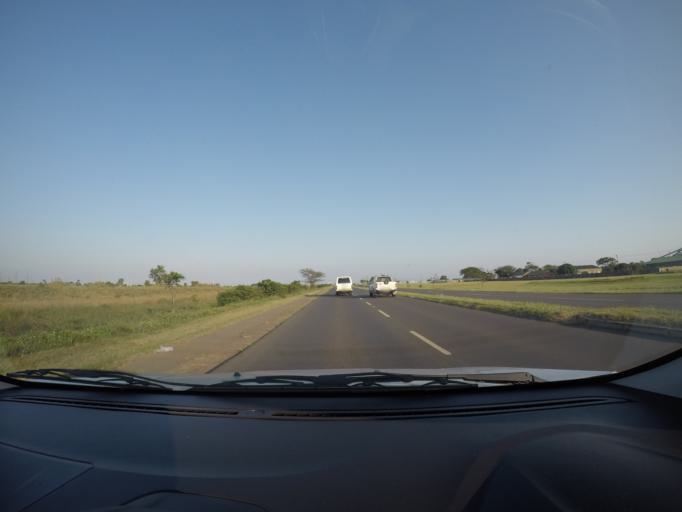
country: ZA
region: KwaZulu-Natal
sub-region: uThungulu District Municipality
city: Richards Bay
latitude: -28.7530
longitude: 32.0334
